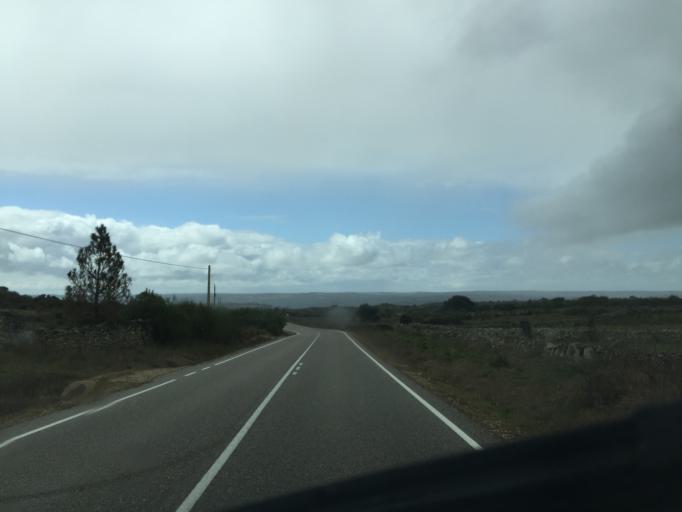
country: ES
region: Castille and Leon
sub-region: Provincia de Zamora
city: Villalcampo
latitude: 41.5175
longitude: -6.0565
